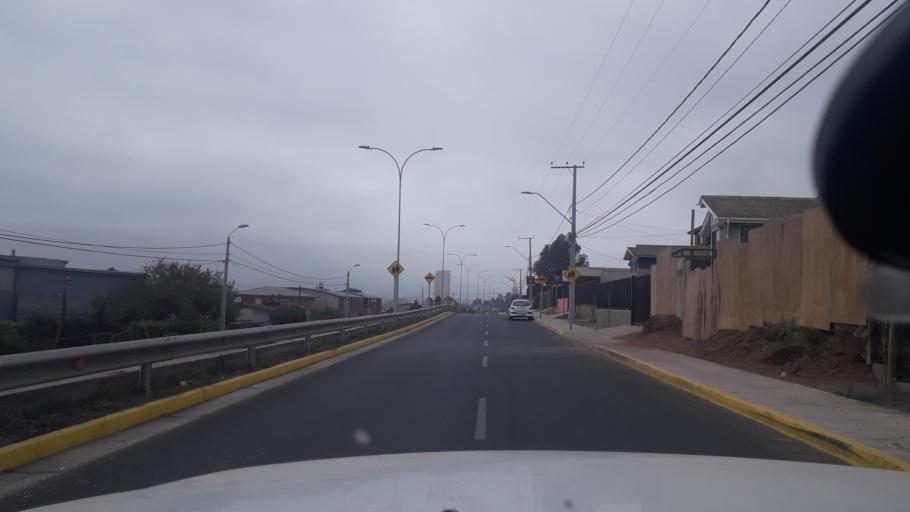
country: CL
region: Valparaiso
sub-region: Provincia de Valparaiso
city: Vina del Mar
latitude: -32.9368
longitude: -71.5327
